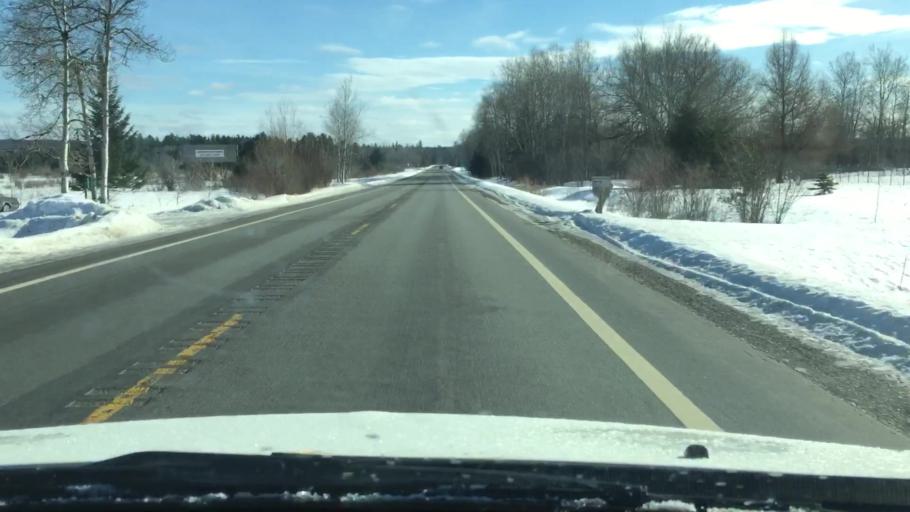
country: US
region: Michigan
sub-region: Charlevoix County
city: East Jordan
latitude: 45.0640
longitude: -85.0812
